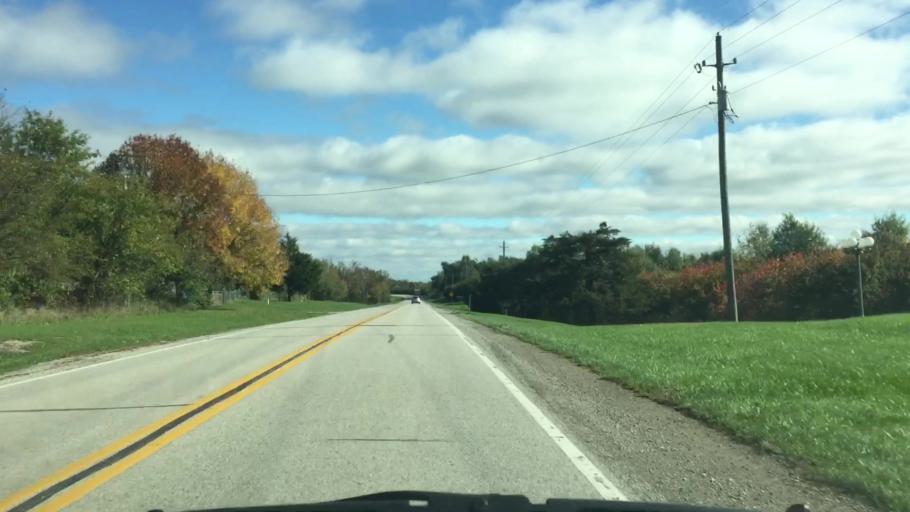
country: US
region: Iowa
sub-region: Decatur County
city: Leon
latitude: 40.7007
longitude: -93.7708
